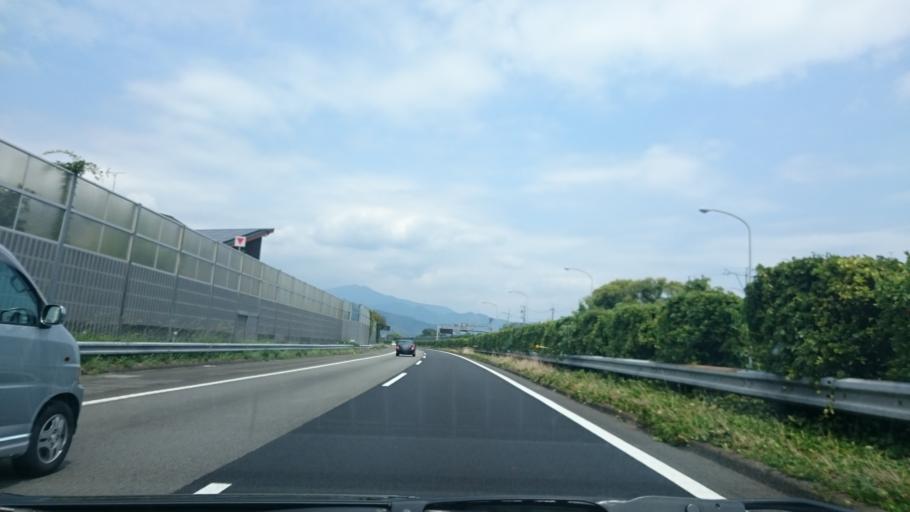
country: JP
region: Shizuoka
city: Shizuoka-shi
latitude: 34.9876
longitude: 138.4355
